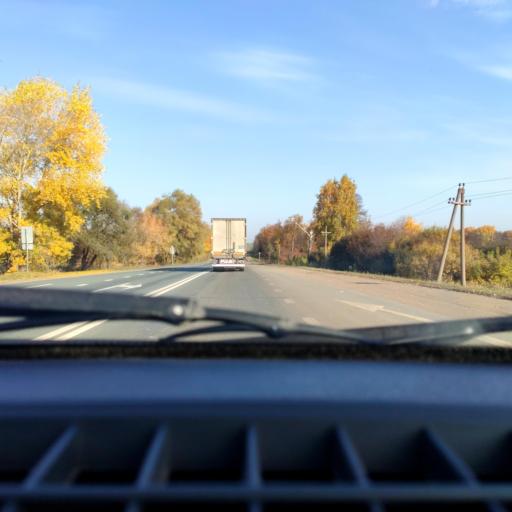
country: RU
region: Bashkortostan
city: Avdon
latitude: 54.7182
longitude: 55.7769
